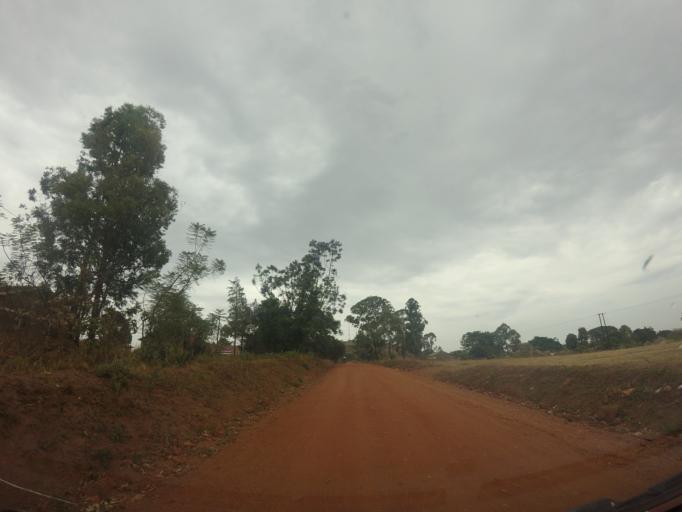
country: UG
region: Northern Region
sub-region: Zombo District
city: Zombo
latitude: 2.7603
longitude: 30.8530
